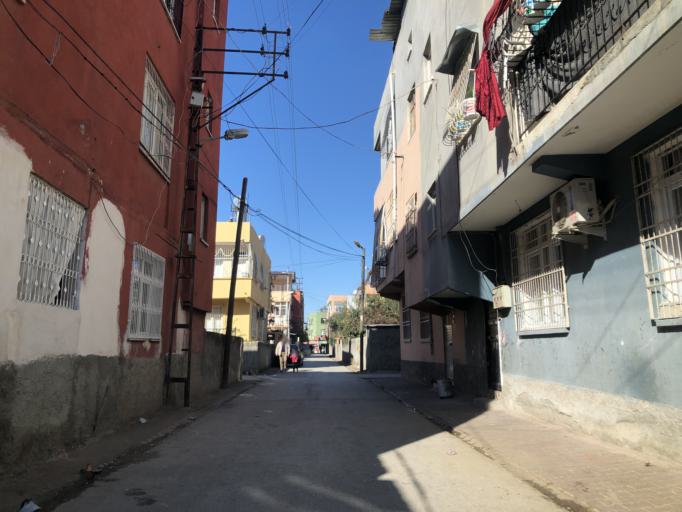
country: TR
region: Adana
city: Yuregir
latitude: 37.0076
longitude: 35.3660
